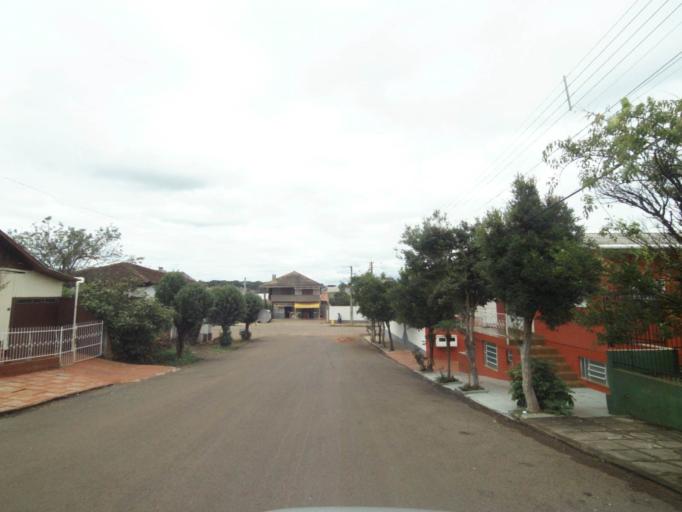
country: BR
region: Rio Grande do Sul
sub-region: Lagoa Vermelha
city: Lagoa Vermelha
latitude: -28.2144
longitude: -51.5341
